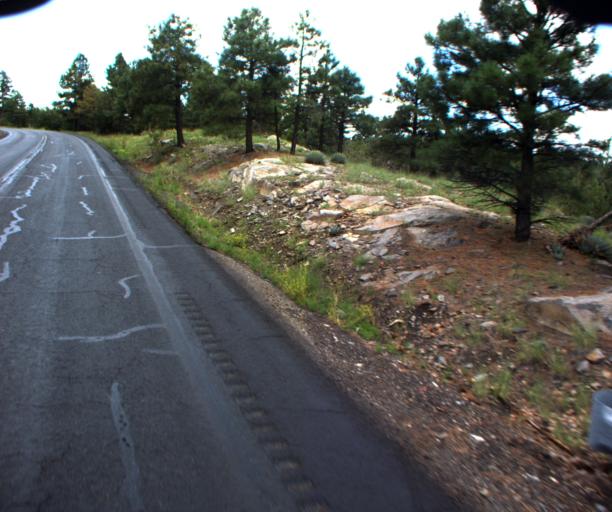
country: US
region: Arizona
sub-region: Gila County
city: Pine
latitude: 34.5144
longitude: -111.4887
